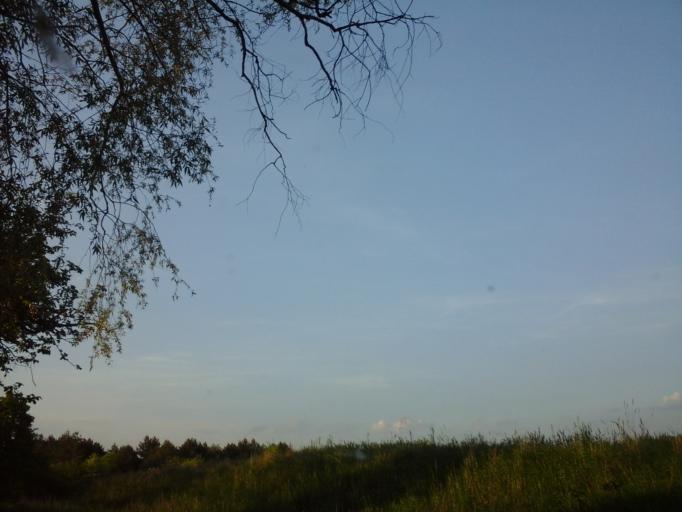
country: PL
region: West Pomeranian Voivodeship
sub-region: Powiat choszczenski
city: Choszczno
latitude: 53.1910
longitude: 15.4169
